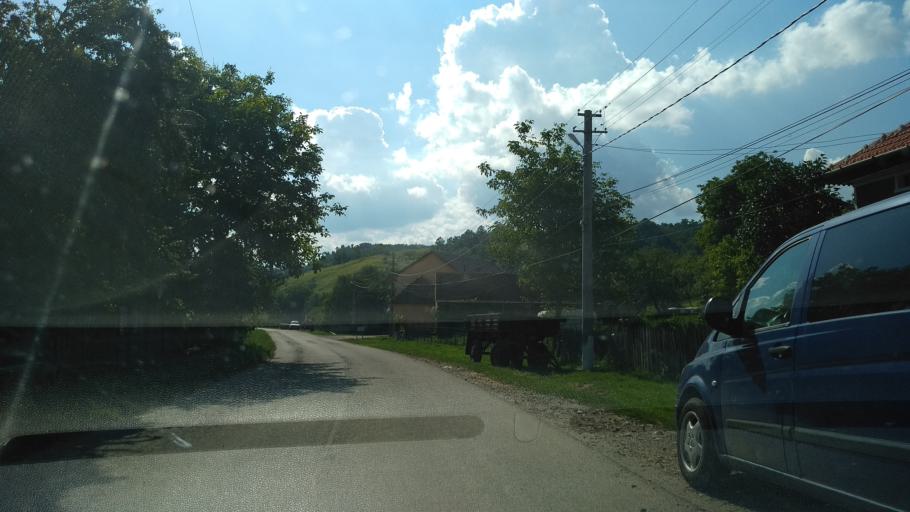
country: RO
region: Hunedoara
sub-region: Comuna Bosorod
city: Bosorod
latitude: 45.7121
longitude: 23.1206
